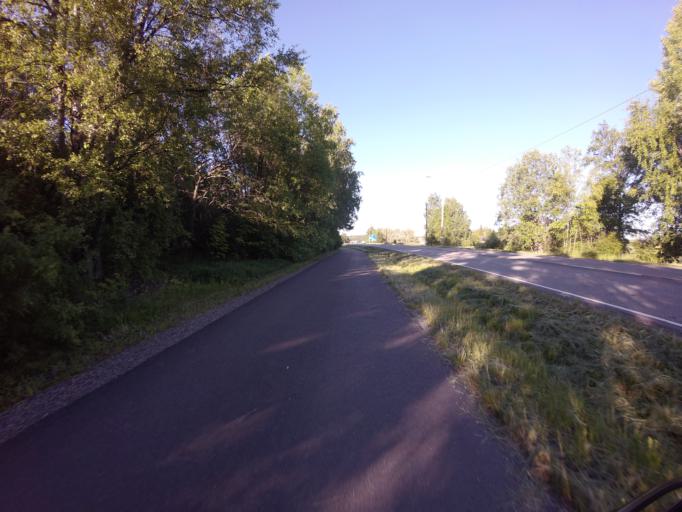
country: FI
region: Varsinais-Suomi
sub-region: Turku
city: Turku
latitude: 60.4905
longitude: 22.3282
